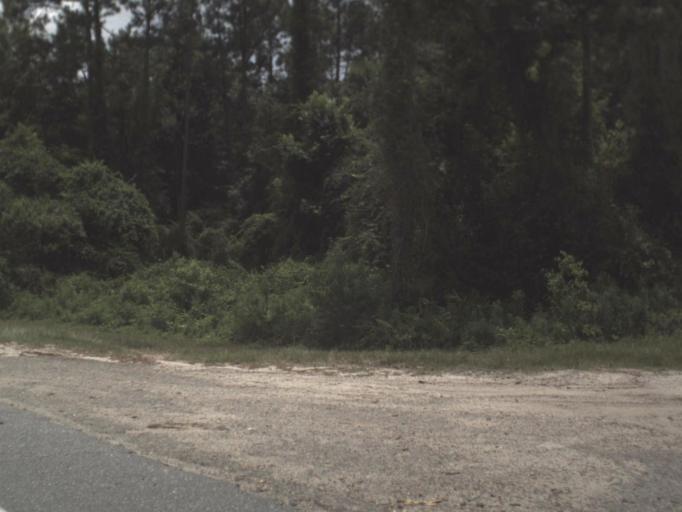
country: US
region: Florida
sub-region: Taylor County
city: Perry
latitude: 30.0847
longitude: -83.5263
